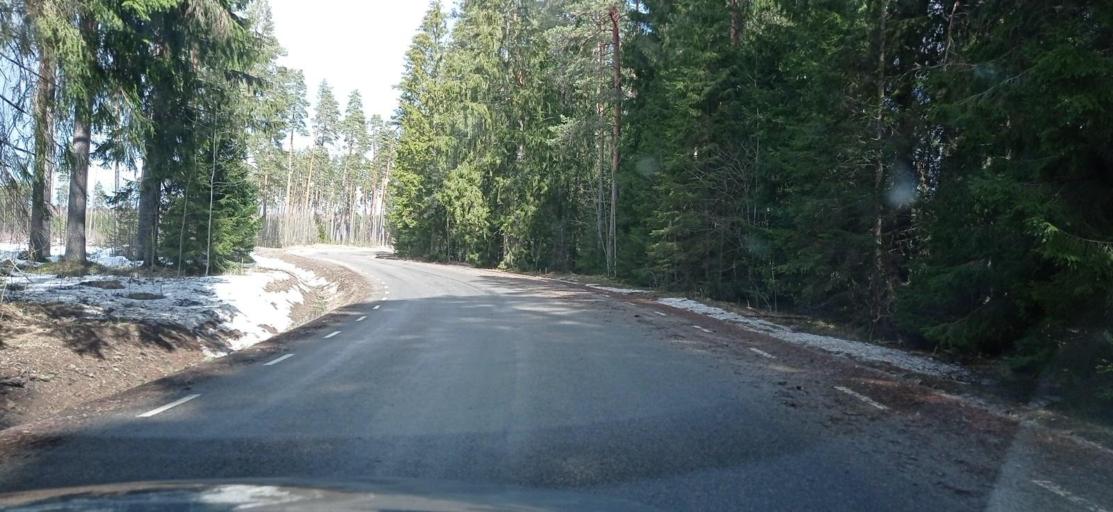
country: EE
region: Polvamaa
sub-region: Polva linn
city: Polva
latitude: 58.1482
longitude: 27.0405
